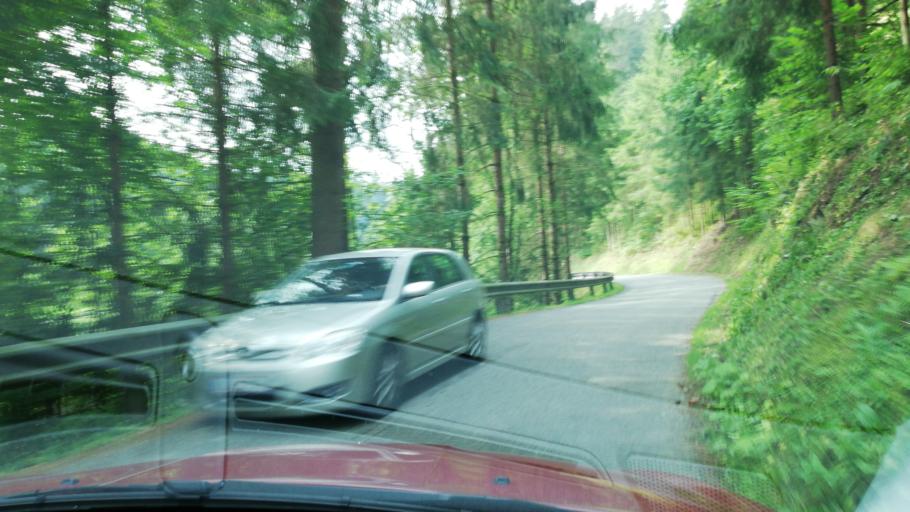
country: AT
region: Upper Austria
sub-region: Politischer Bezirk Rohrbach
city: Kleinzell im Muehlkreis
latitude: 48.4981
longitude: 14.0092
